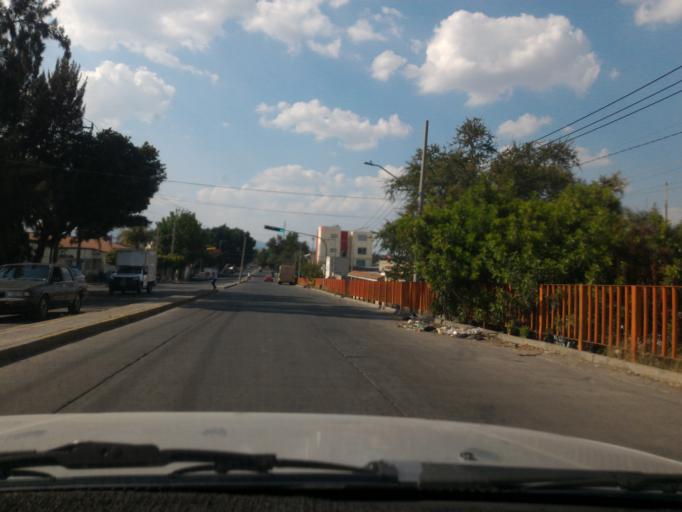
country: MX
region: Jalisco
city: Guadalajara
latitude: 20.6229
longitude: -103.3817
